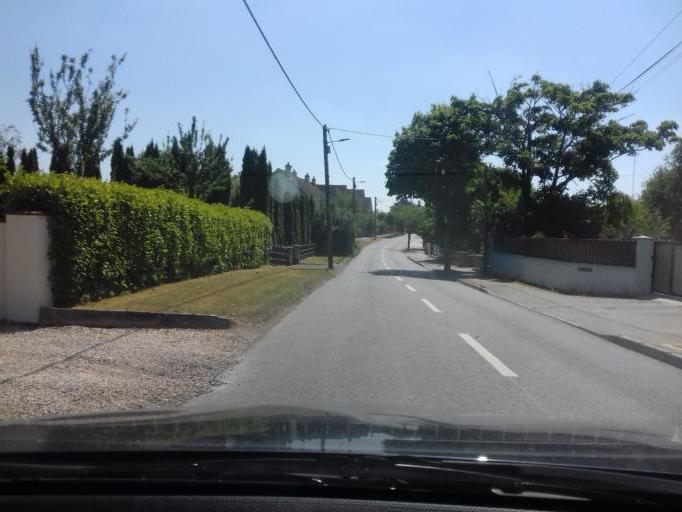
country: IE
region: Leinster
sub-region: An Mhi
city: Ashbourne
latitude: 53.5221
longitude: -6.3156
